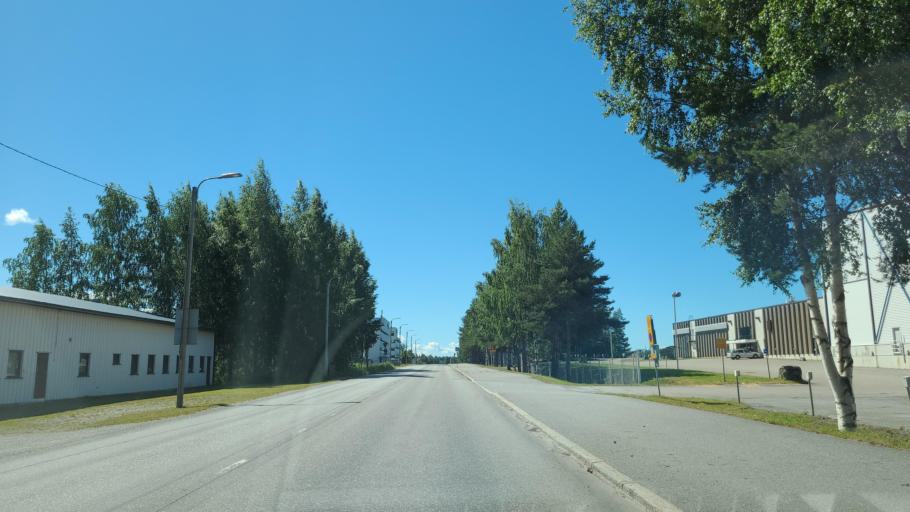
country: FI
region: Ostrobothnia
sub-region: Vaasa
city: Ristinummi
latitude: 63.0598
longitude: 21.7335
